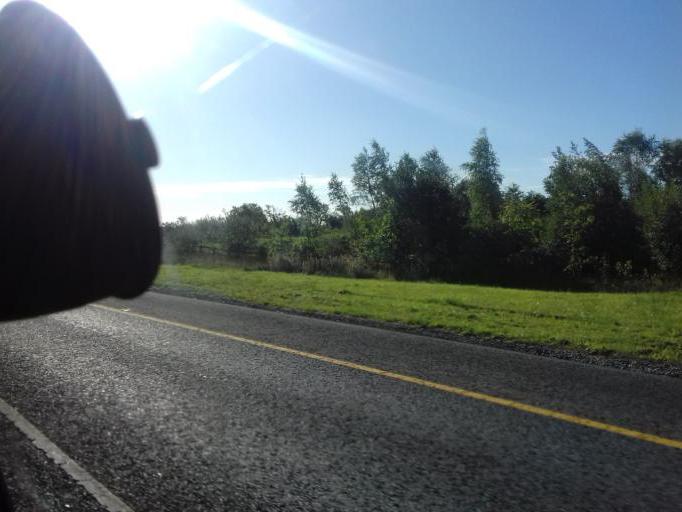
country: IE
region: Leinster
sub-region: An Iarmhi
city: Kinnegad
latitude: 53.4429
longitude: -7.0382
